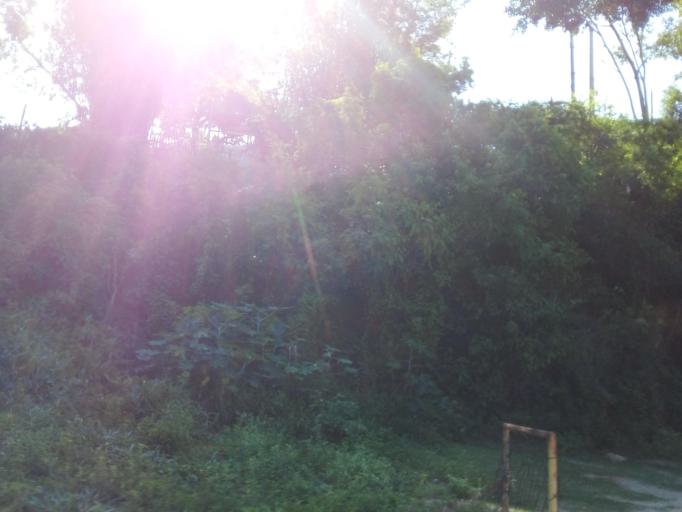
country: BR
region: Espirito Santo
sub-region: Vitoria
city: Vitoria
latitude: -20.2816
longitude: -40.3766
